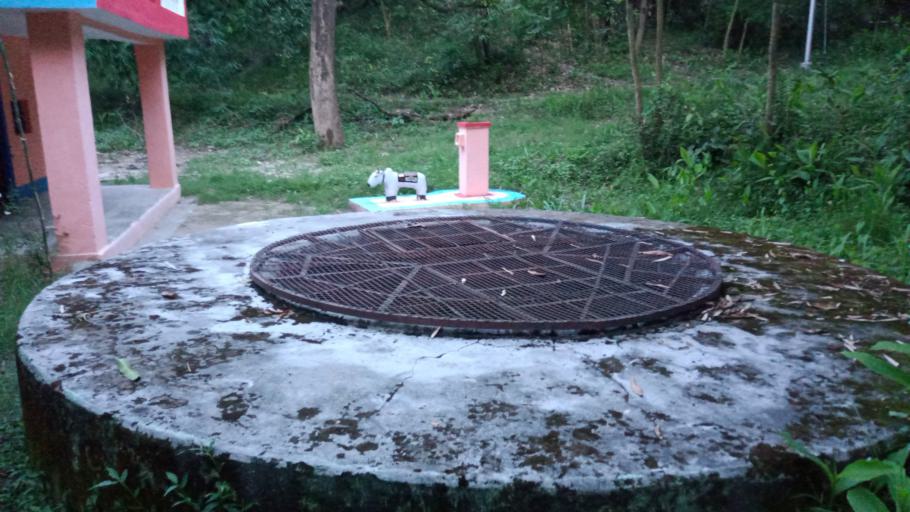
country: IN
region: Himachal Pradesh
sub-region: Hamirpur
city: Nadaun
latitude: 31.6941
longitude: 76.3583
